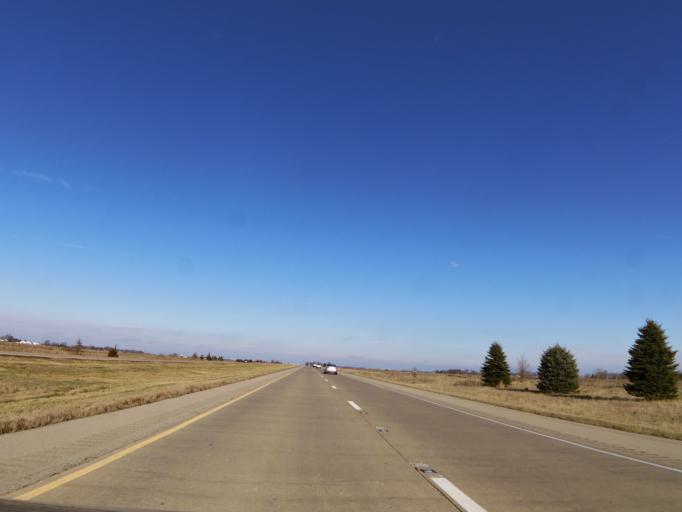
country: US
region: Illinois
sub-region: LaSalle County
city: La Salle
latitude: 41.4253
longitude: -89.0585
